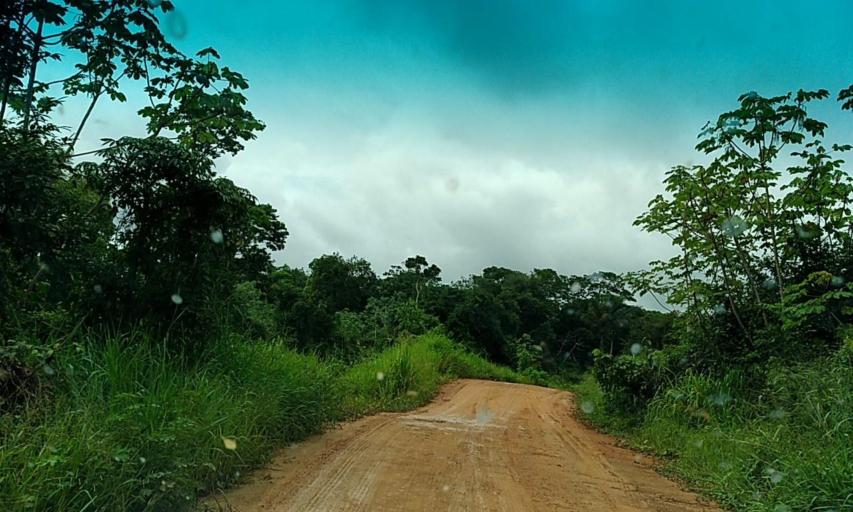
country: BR
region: Para
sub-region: Altamira
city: Altamira
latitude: -3.0824
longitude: -51.7026
